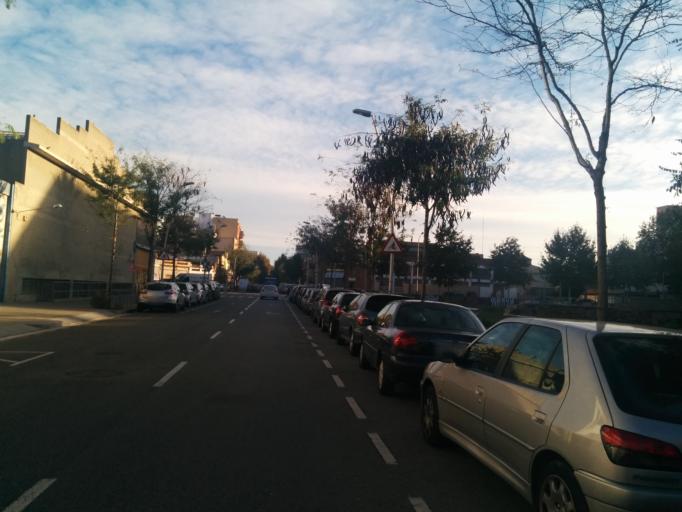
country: ES
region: Catalonia
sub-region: Provincia de Barcelona
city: Sant Marti
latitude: 41.4097
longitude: 2.2066
